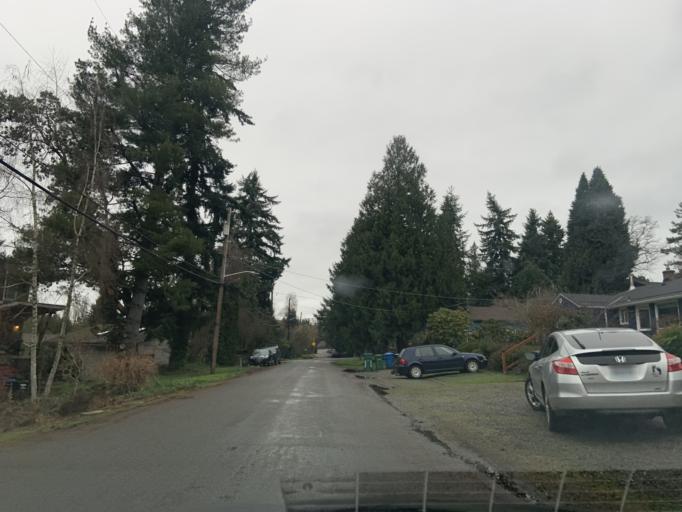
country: US
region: Washington
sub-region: King County
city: Lake Forest Park
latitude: 47.7112
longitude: -122.2840
